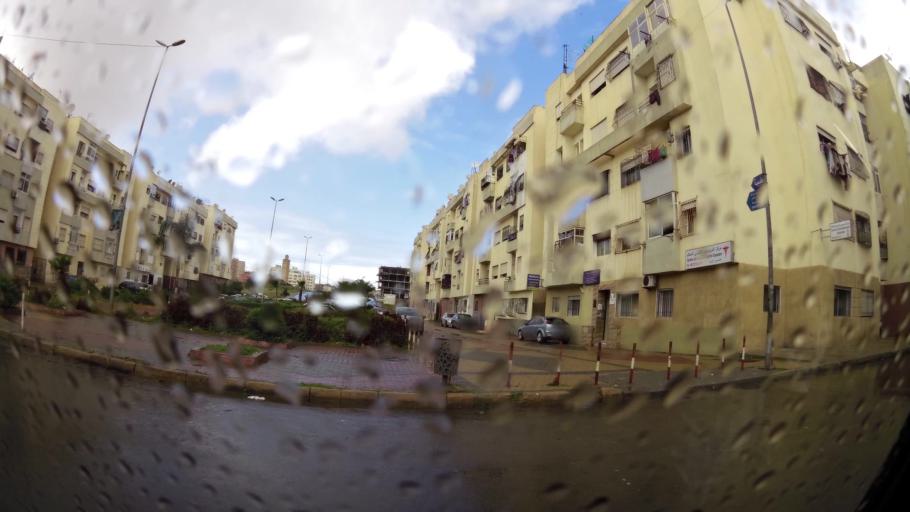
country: MA
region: Grand Casablanca
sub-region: Casablanca
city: Casablanca
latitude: 33.5451
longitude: -7.6763
